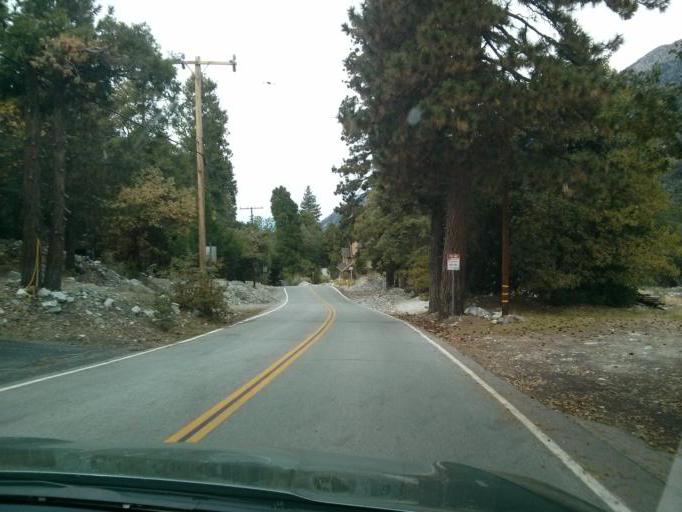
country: US
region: California
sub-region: Riverside County
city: Cherry Valley
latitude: 34.0825
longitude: -116.8984
